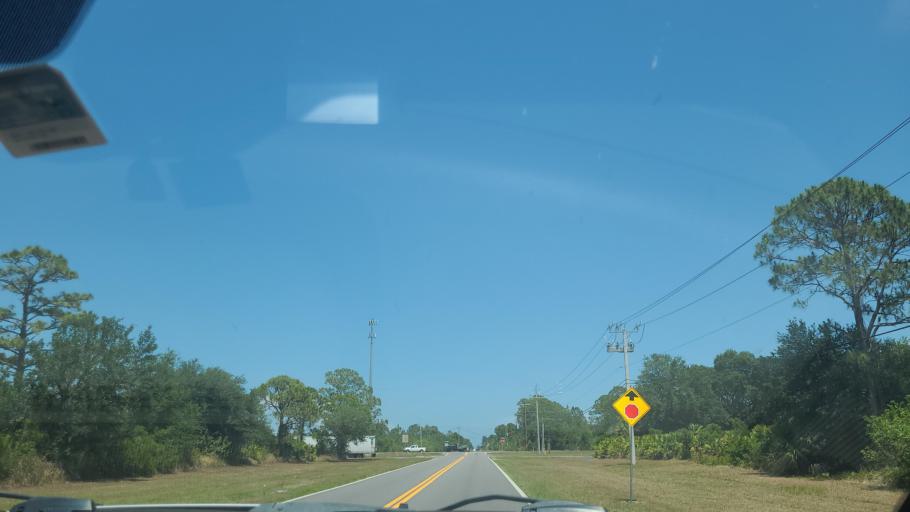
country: US
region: Florida
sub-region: Brevard County
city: Grant-Valkaria
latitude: 27.9245
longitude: -80.6247
